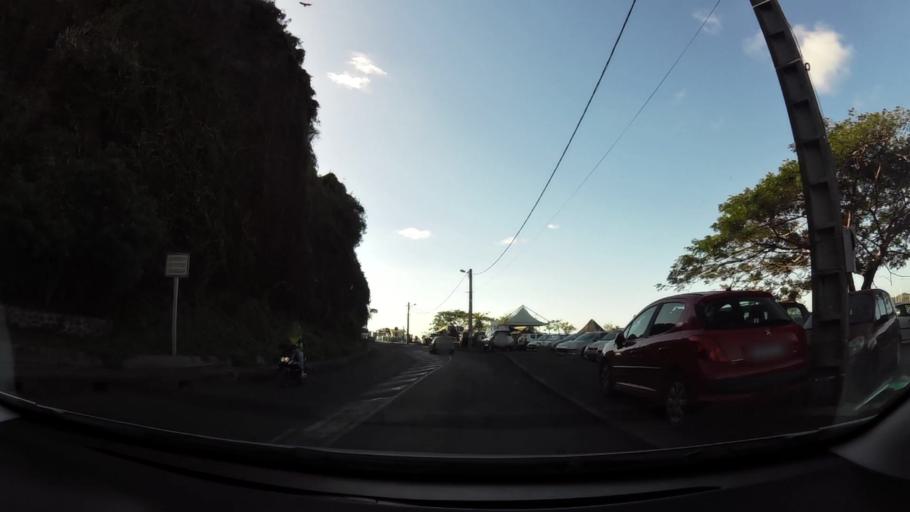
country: YT
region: Dzaoudzi
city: Dzaoudzi
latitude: -12.7832
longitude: 45.2580
